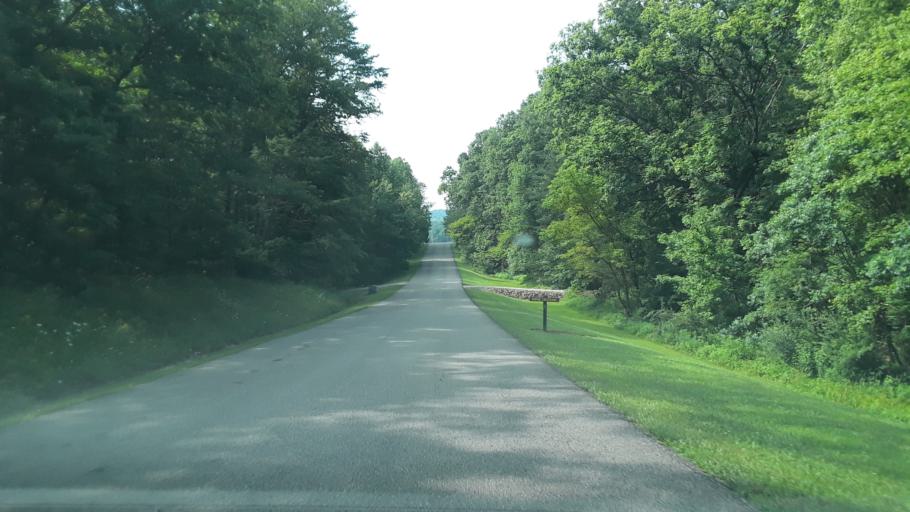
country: US
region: Indiana
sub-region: Clark County
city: Henryville
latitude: 38.4608
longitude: -85.8654
